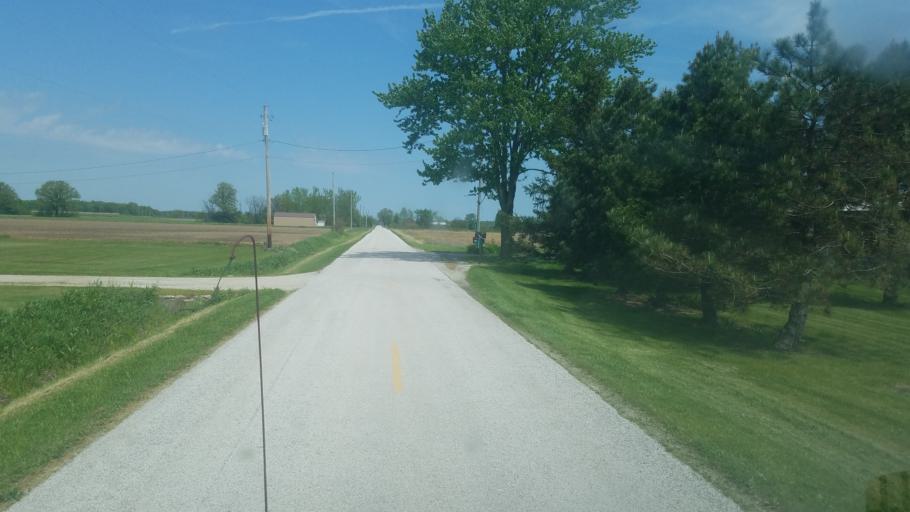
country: US
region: Ohio
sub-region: Ottawa County
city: Oak Harbor
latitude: 41.4776
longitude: -83.2019
